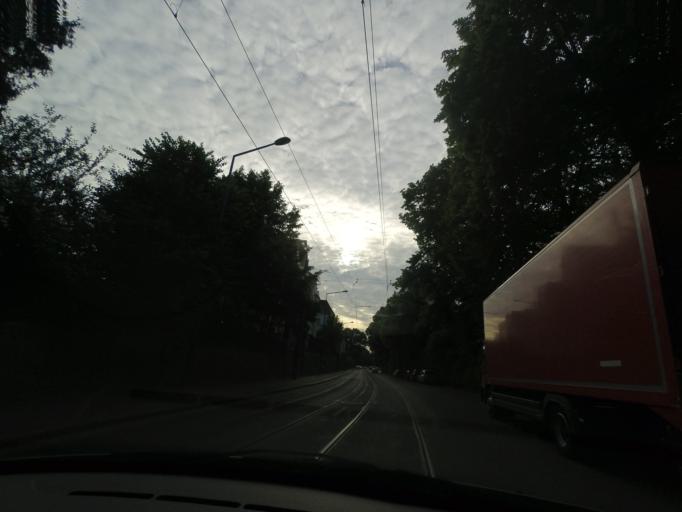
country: DE
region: Saxony
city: Heidenau
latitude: 51.0334
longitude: 13.8263
